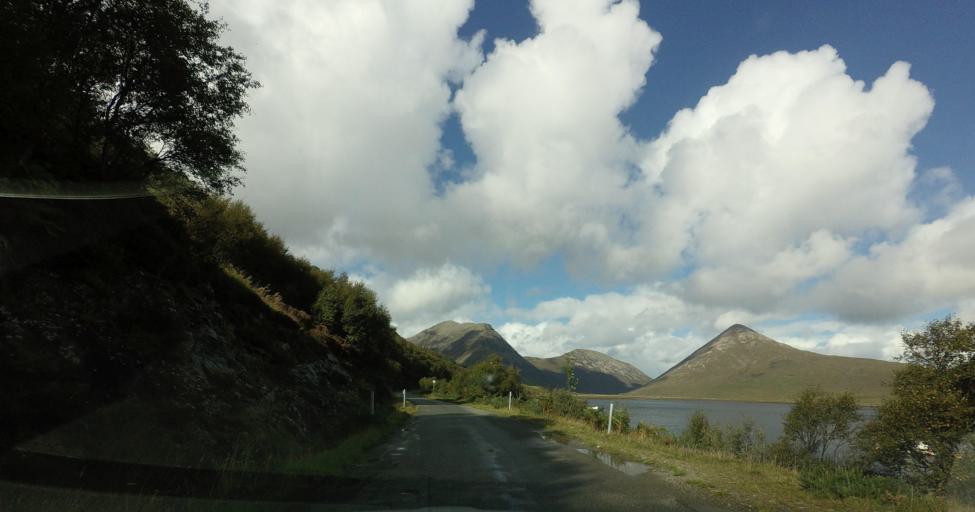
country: GB
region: Scotland
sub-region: Highland
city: Portree
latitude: 57.2106
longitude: -6.0335
